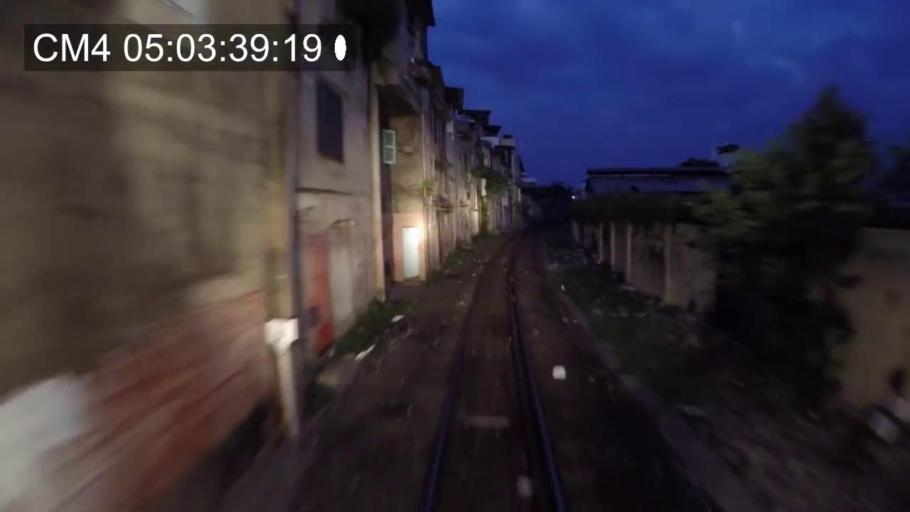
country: VN
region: Khanh Hoa
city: Nha Trang
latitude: 12.2577
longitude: 109.1713
